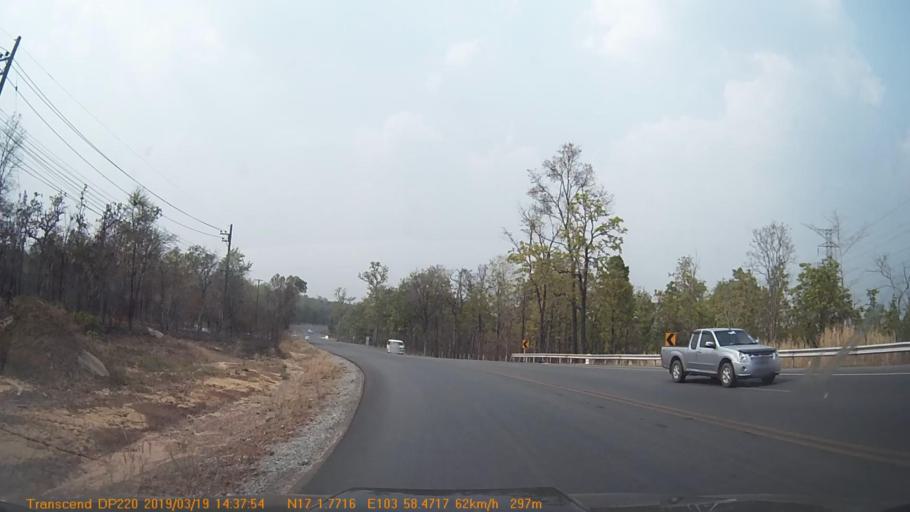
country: TH
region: Sakon Nakhon
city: Phu Phan
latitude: 17.0298
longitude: 103.9745
